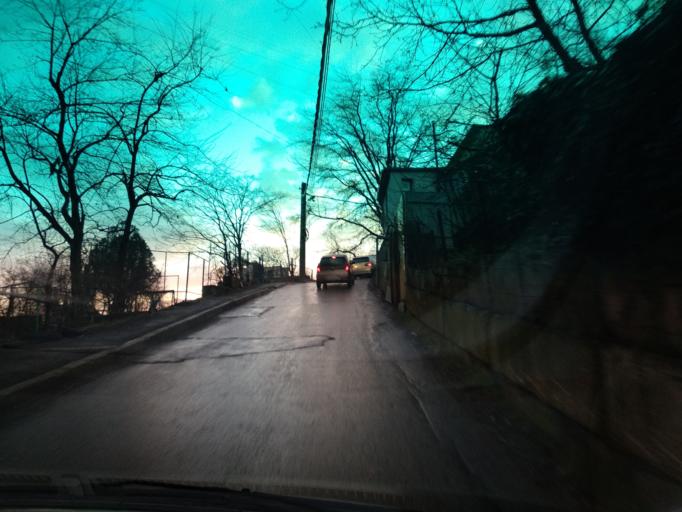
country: RU
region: Krasnodarskiy
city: Tuapse
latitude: 44.1067
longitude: 39.0816
